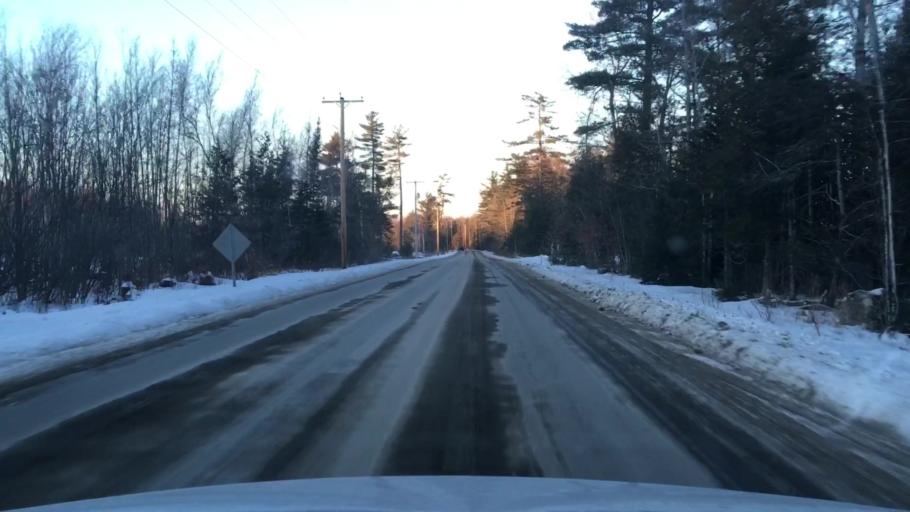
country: US
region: Maine
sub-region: Penobscot County
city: Orrington
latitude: 44.7096
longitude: -68.7540
